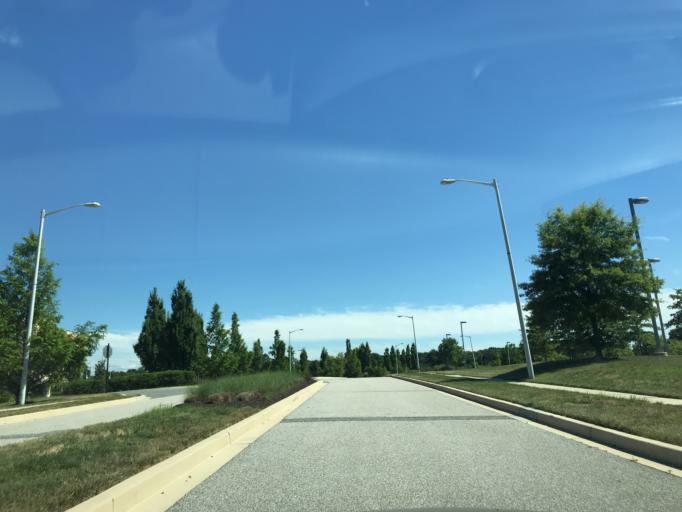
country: US
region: Maryland
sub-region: Harford County
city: Aberdeen
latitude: 39.5037
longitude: -76.1486
